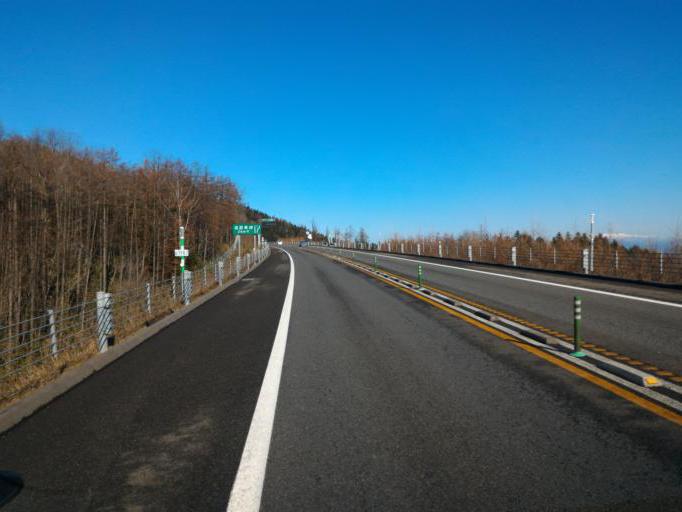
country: JP
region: Hokkaido
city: Otofuke
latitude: 43.0490
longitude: 142.7845
